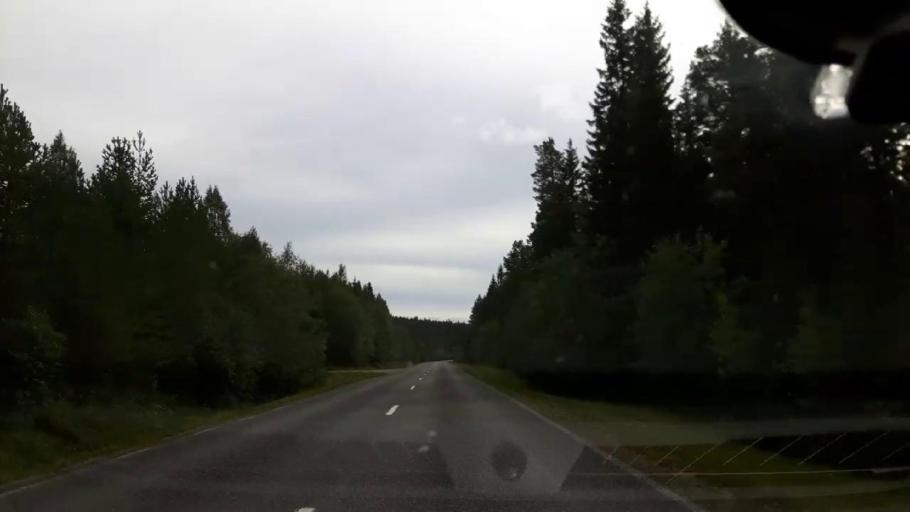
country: SE
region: Jaemtland
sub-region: Ragunda Kommun
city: Hammarstrand
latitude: 63.0644
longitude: 15.9228
